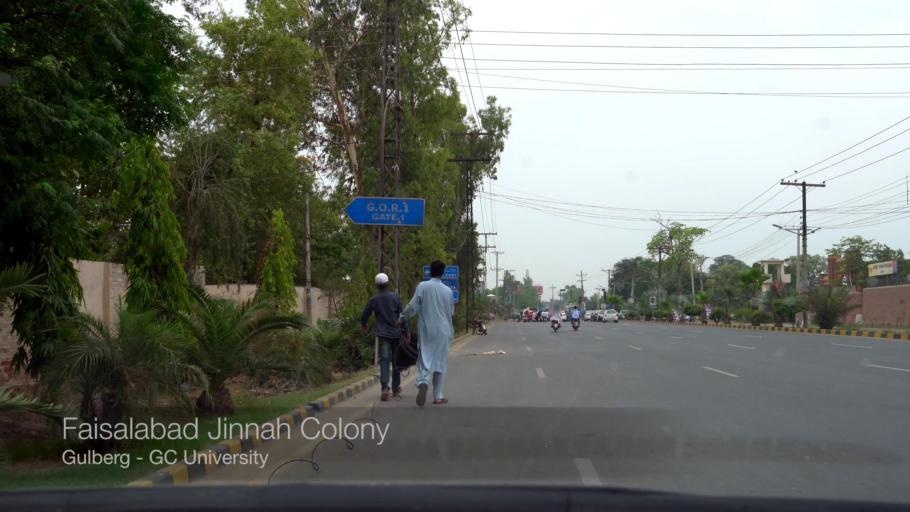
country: PK
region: Punjab
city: Faisalabad
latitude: 31.4290
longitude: 73.0759
